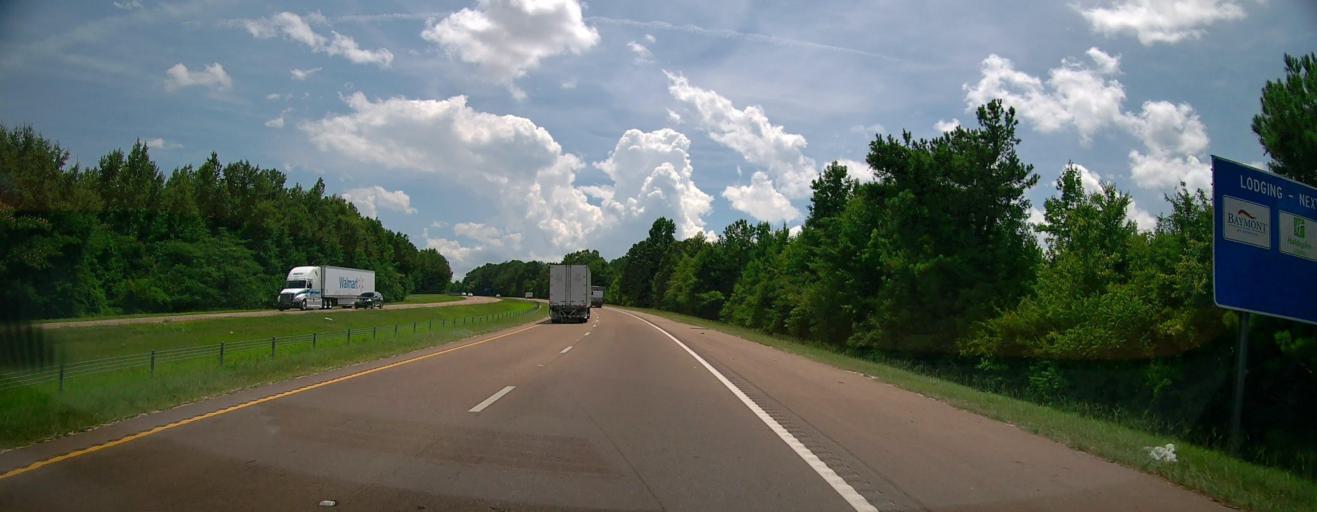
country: US
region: Mississippi
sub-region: Lee County
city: Tupelo
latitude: 34.2856
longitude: -88.7074
